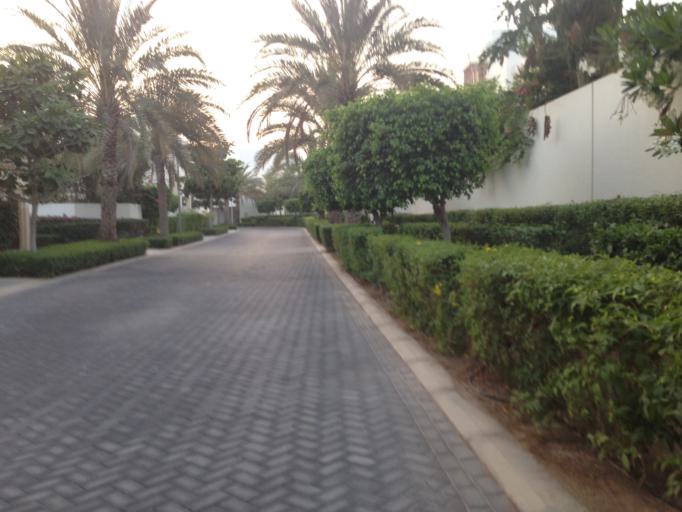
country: OM
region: Muhafazat Masqat
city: As Sib al Jadidah
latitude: 23.6273
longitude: 58.2710
